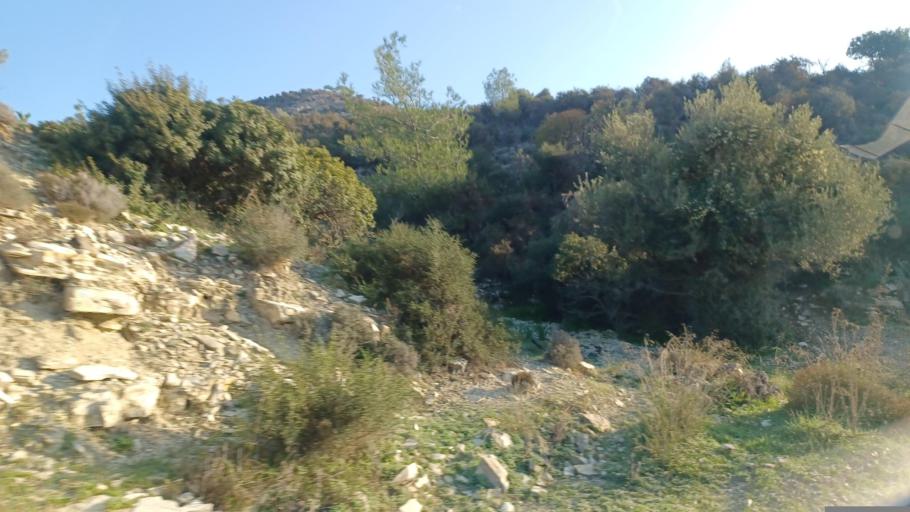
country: CY
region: Larnaka
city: Kofinou
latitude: 34.8164
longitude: 33.3189
